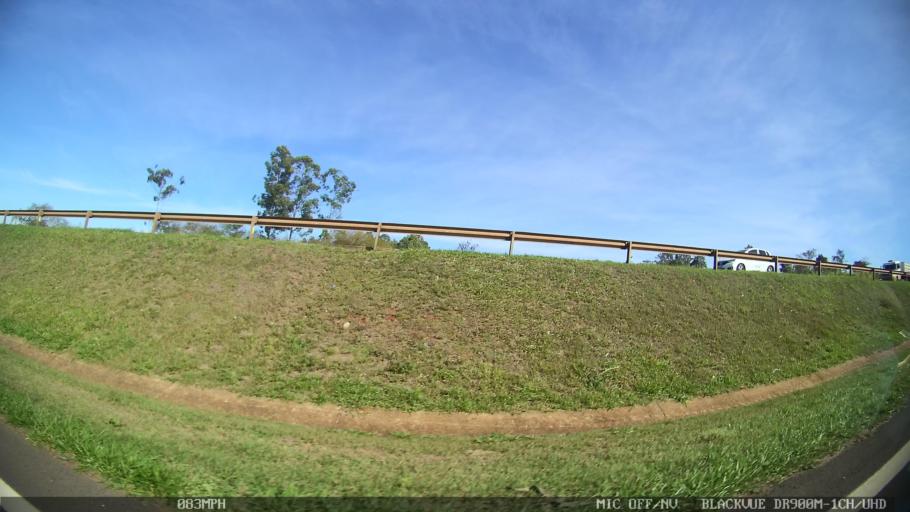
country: BR
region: Sao Paulo
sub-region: Pirassununga
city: Pirassununga
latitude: -22.0911
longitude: -47.4184
